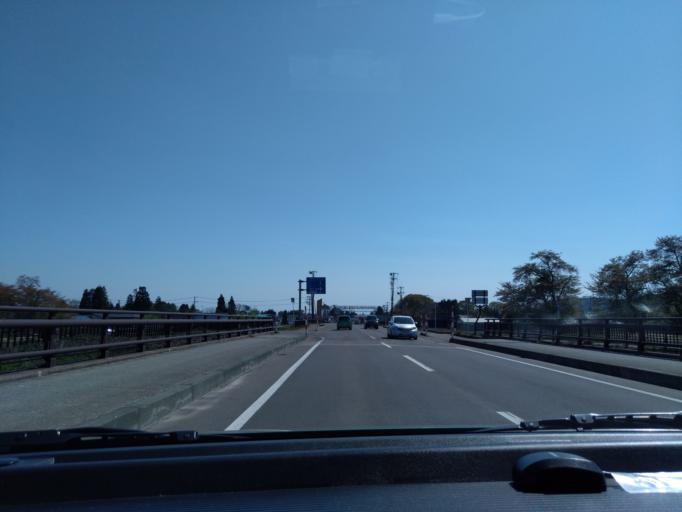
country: JP
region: Akita
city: Kakunodatemachi
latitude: 39.5791
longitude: 140.5672
